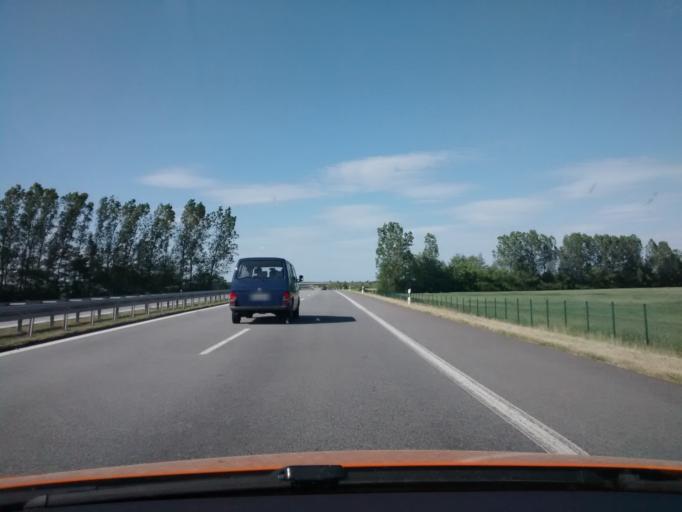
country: DE
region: Brandenburg
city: Trebbin
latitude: 52.1694
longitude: 13.2427
